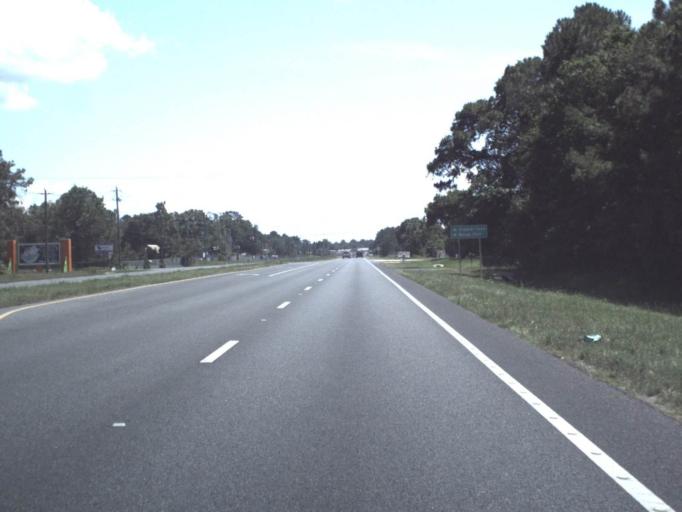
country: US
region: Florida
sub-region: Putnam County
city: Palatka
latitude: 29.6766
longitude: -81.6597
